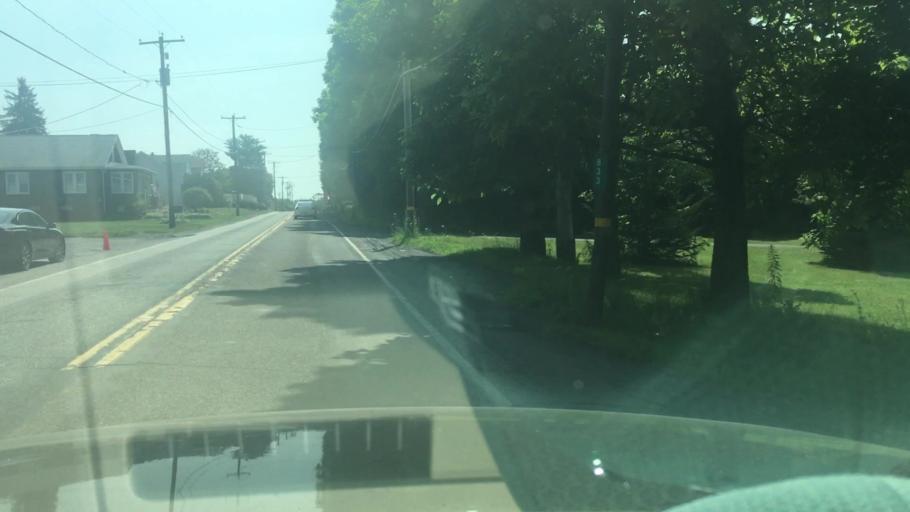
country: US
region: Pennsylvania
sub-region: Schuylkill County
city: Hometown
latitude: 40.8174
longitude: -76.0515
